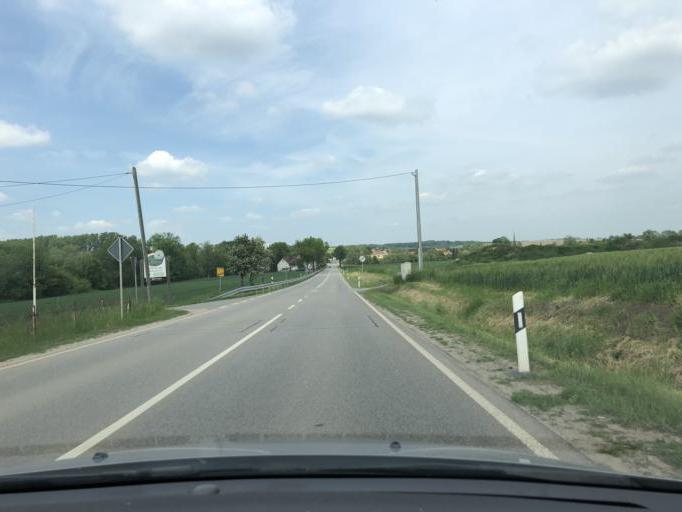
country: DE
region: Thuringia
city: Saara
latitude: 50.9454
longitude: 12.4245
